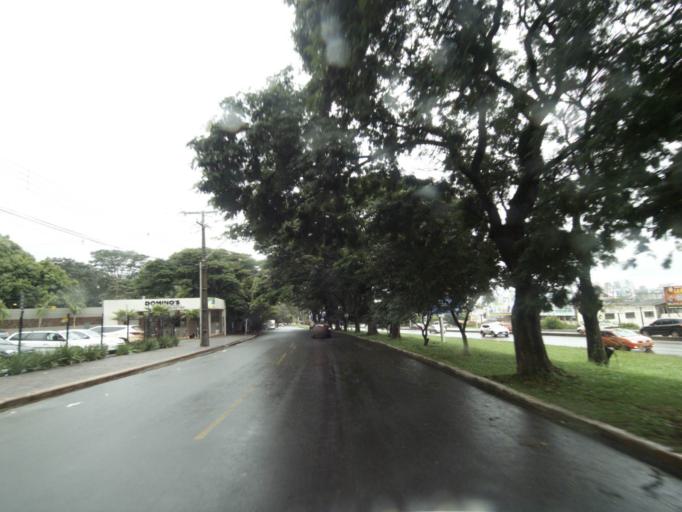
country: PY
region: Alto Parana
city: Ciudad del Este
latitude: -25.5070
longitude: -54.5910
